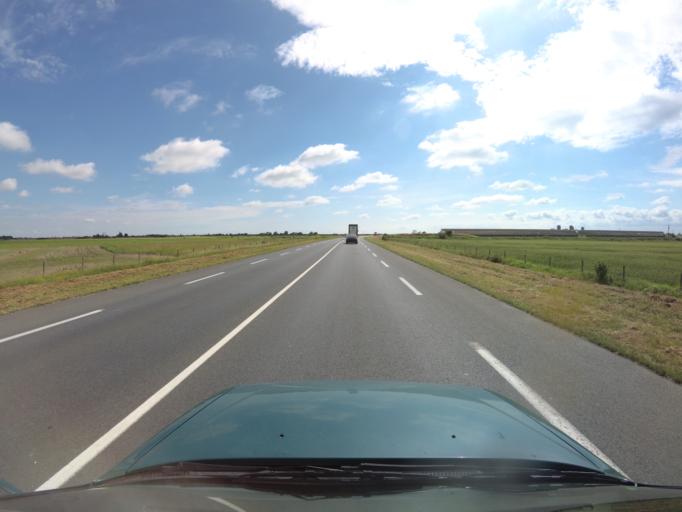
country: FR
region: Pays de la Loire
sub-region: Departement de la Vendee
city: Champagne-les-Marais
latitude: 46.4246
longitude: -1.0953
